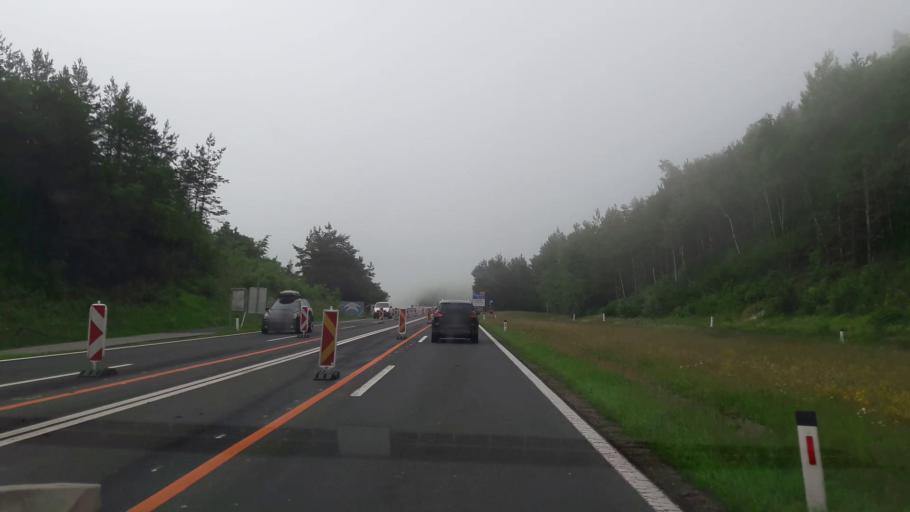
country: AT
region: Burgenland
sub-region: Politischer Bezirk Mattersburg
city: Sieggraben
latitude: 47.6721
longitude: 16.3799
